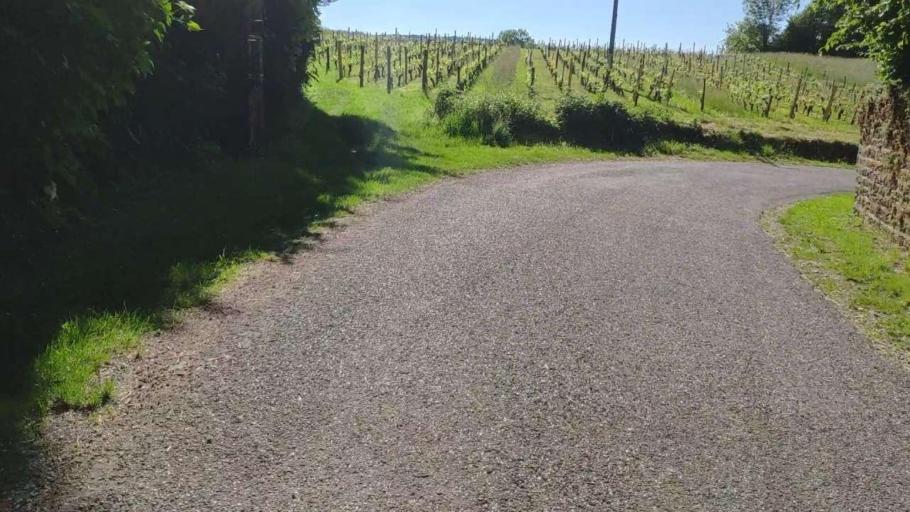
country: FR
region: Franche-Comte
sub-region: Departement du Jura
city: Perrigny
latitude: 46.7208
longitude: 5.5770
